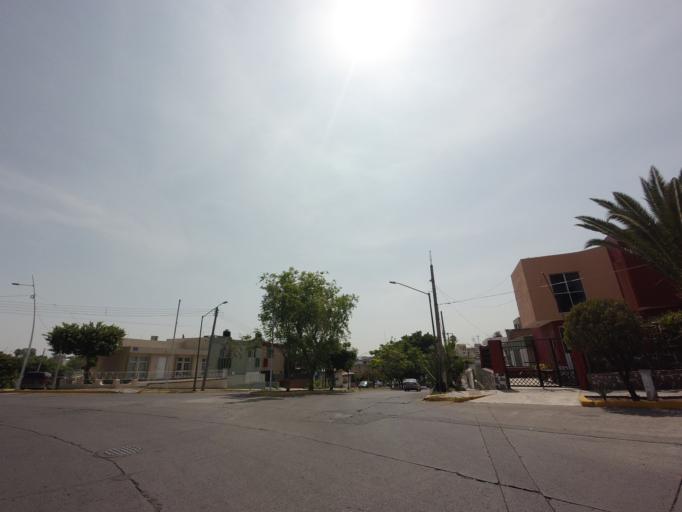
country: MX
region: Jalisco
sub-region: Zapopan
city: Zapopan
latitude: 20.6930
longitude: -103.3424
